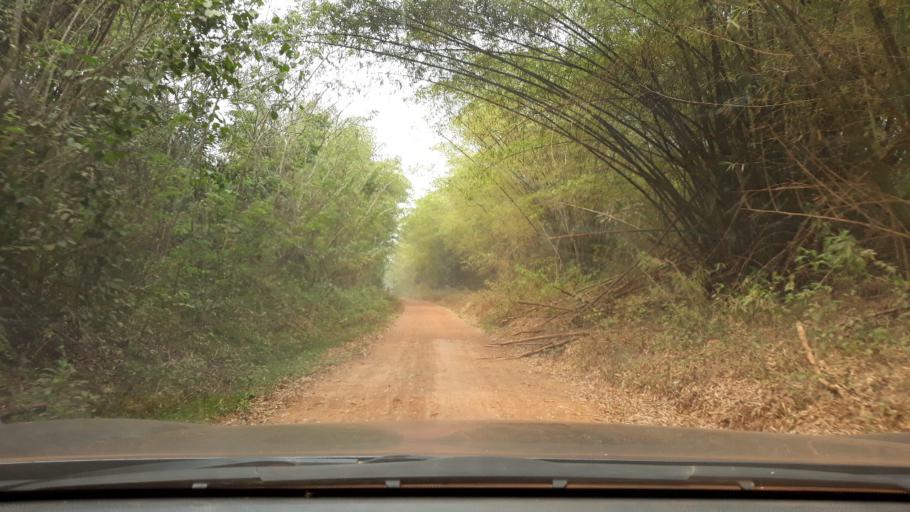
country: CD
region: Eastern Province
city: Aketi
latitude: 2.8188
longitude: 23.8851
